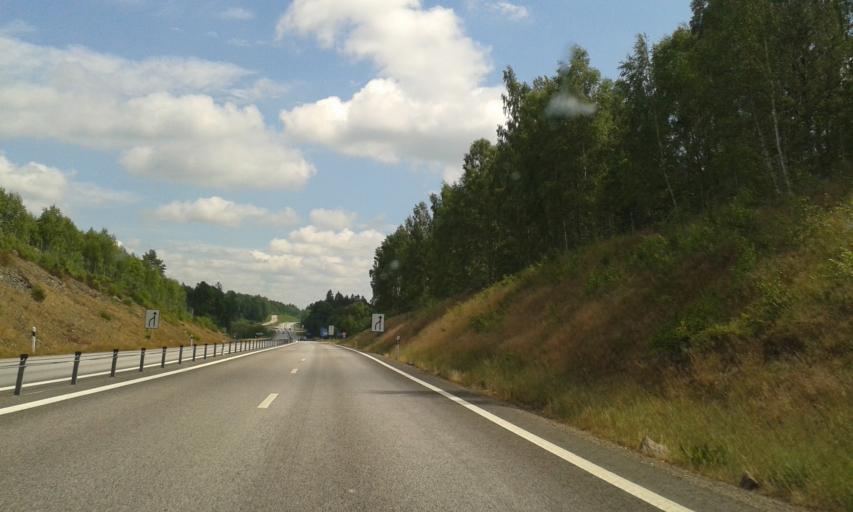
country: SE
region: Kronoberg
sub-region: Alvesta Kommun
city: Alvesta
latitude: 56.9206
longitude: 14.5831
